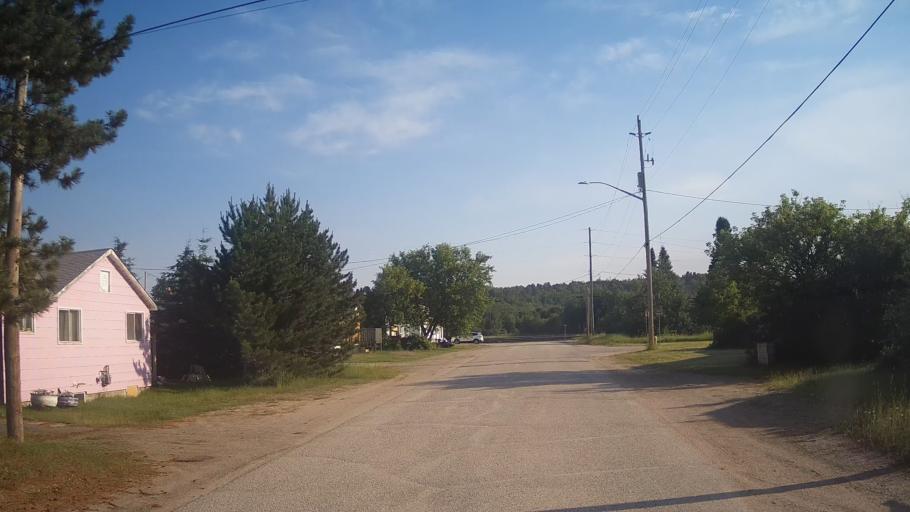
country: CA
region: Ontario
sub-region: Rainy River District
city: Atikokan
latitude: 49.4174
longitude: -91.6659
